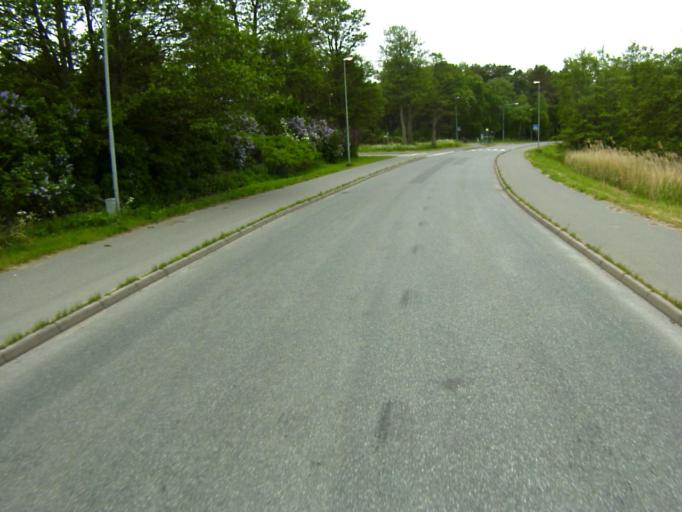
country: SE
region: Skane
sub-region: Kristianstads Kommun
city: Ahus
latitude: 55.9147
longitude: 14.2860
